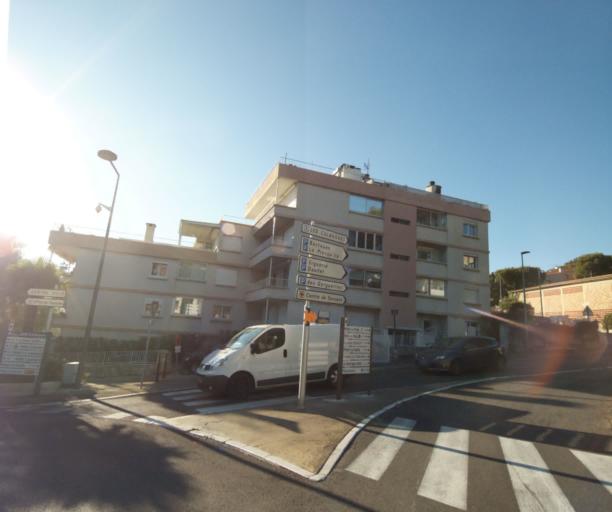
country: FR
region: Provence-Alpes-Cote d'Azur
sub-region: Departement des Bouches-du-Rhone
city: Cassis
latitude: 43.2184
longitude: 5.5394
